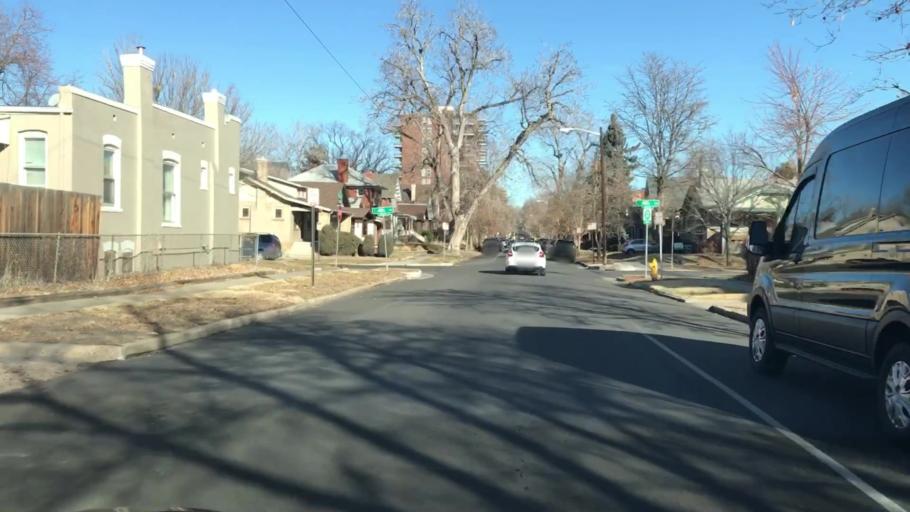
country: US
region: Colorado
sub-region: Denver County
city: Denver
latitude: 39.7221
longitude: -104.9776
